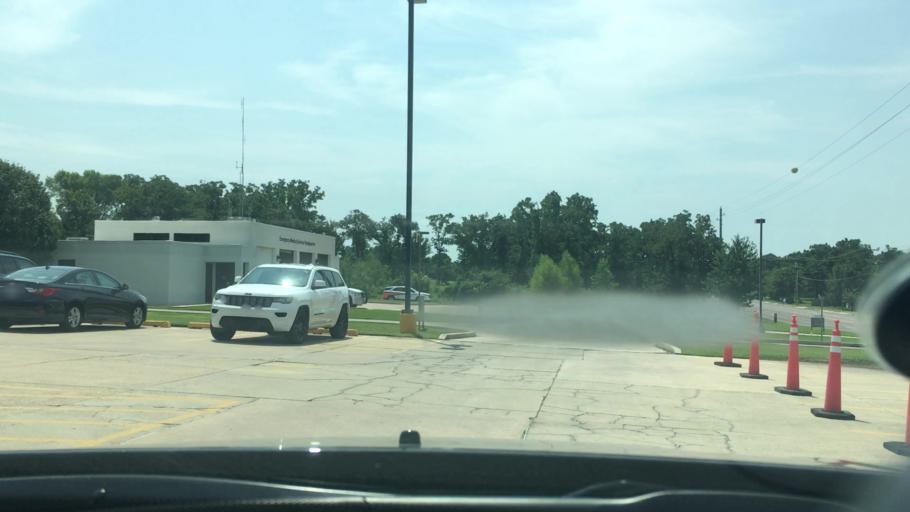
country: US
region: Oklahoma
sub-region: Pontotoc County
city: Ada
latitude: 34.7780
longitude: -96.6345
